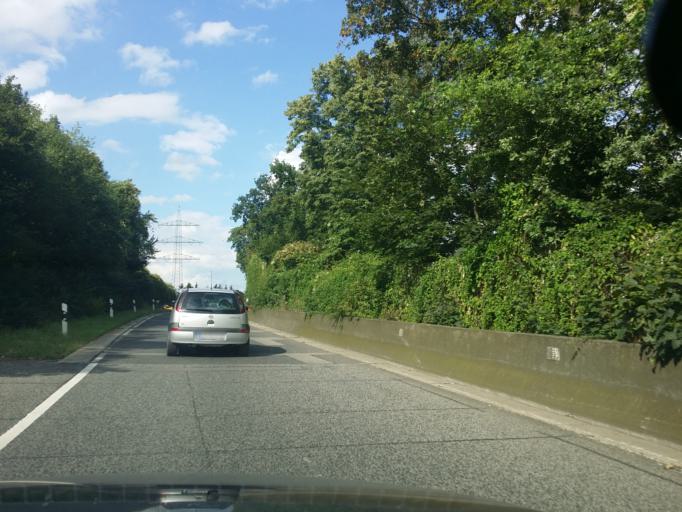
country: DE
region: Hesse
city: Sulzbach
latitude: 50.1114
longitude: 8.5238
